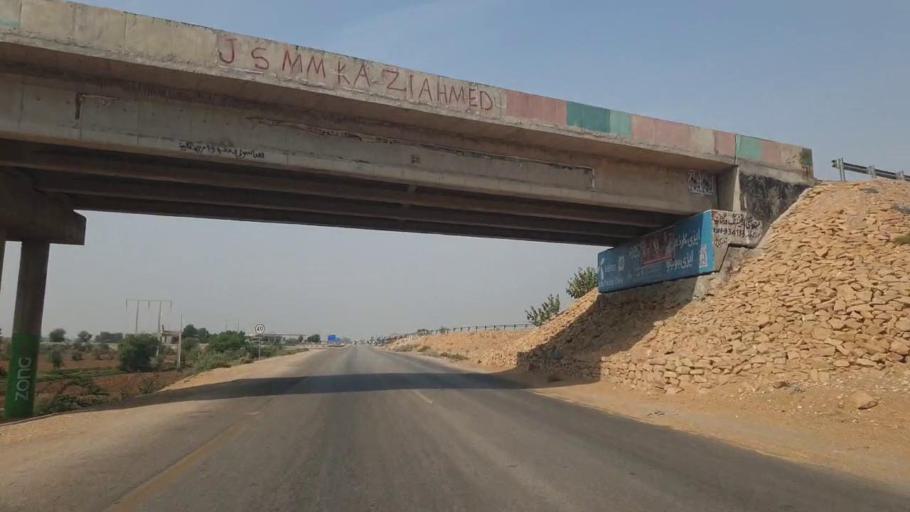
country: PK
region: Sindh
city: Sann
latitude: 26.1555
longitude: 68.0237
